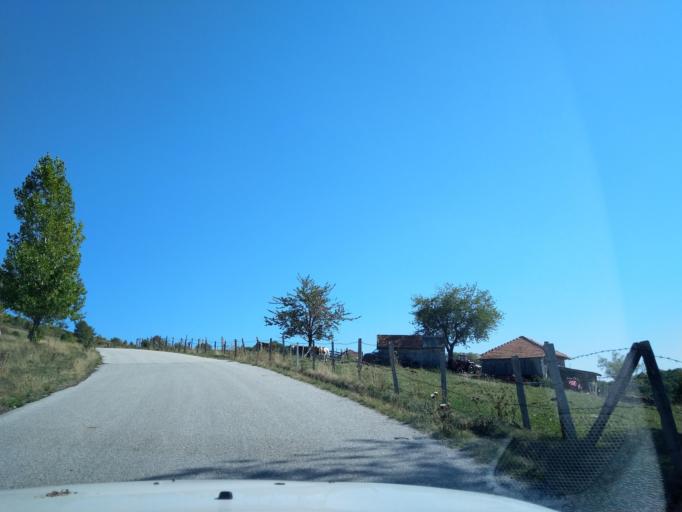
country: RS
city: Sokolovica
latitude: 43.2509
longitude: 20.3197
